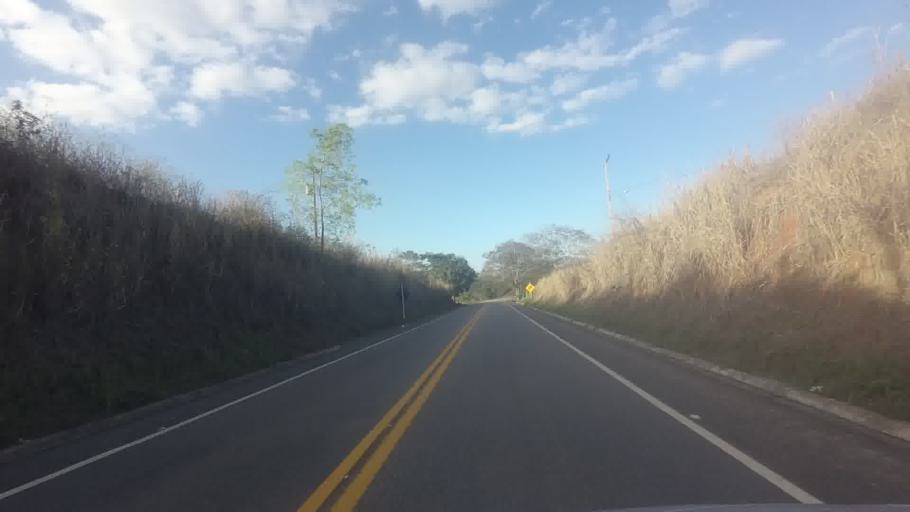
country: BR
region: Espirito Santo
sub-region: Mimoso Do Sul
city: Mimoso do Sul
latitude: -20.9201
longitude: -41.3085
